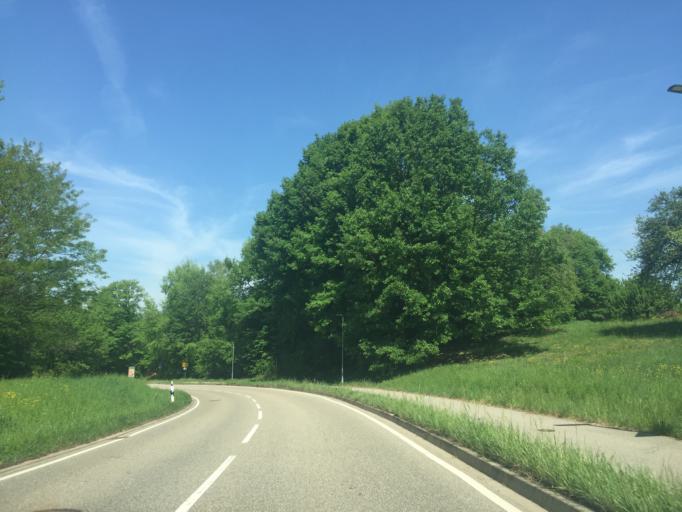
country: DE
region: Baden-Wuerttemberg
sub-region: Karlsruhe Region
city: Malsch
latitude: 48.8728
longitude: 8.3455
